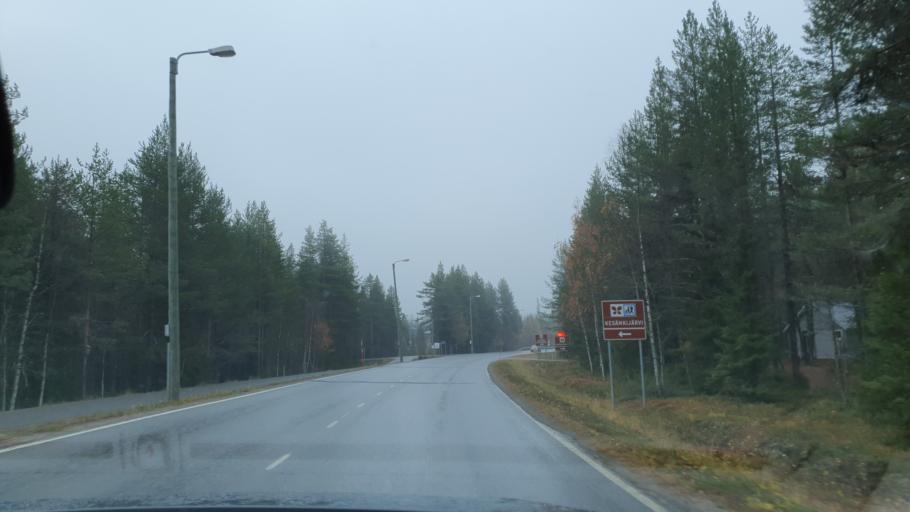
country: FI
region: Lapland
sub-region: Tunturi-Lappi
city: Kolari
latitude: 67.6026
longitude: 24.1710
